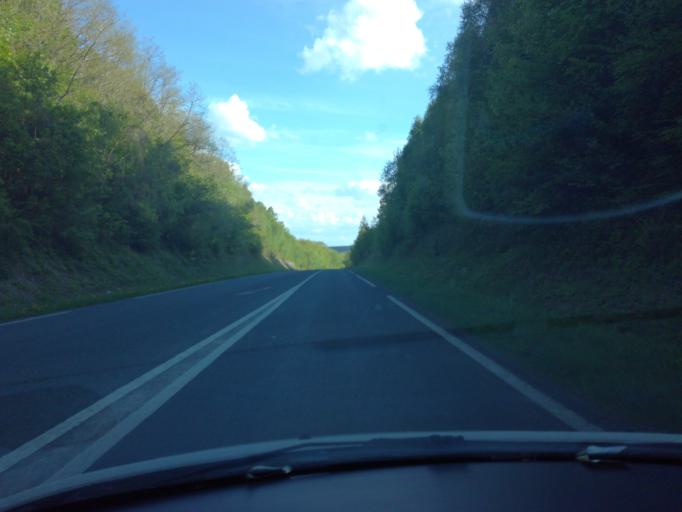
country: FR
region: Picardie
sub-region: Departement de la Somme
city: Poix-de-Picardie
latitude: 49.7892
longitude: 1.9803
